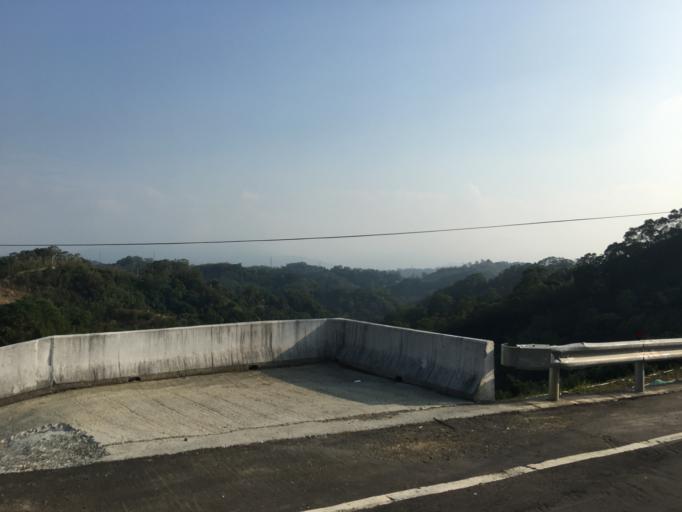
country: TW
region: Taiwan
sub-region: Hsinchu
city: Hsinchu
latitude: 24.7404
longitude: 121.0393
